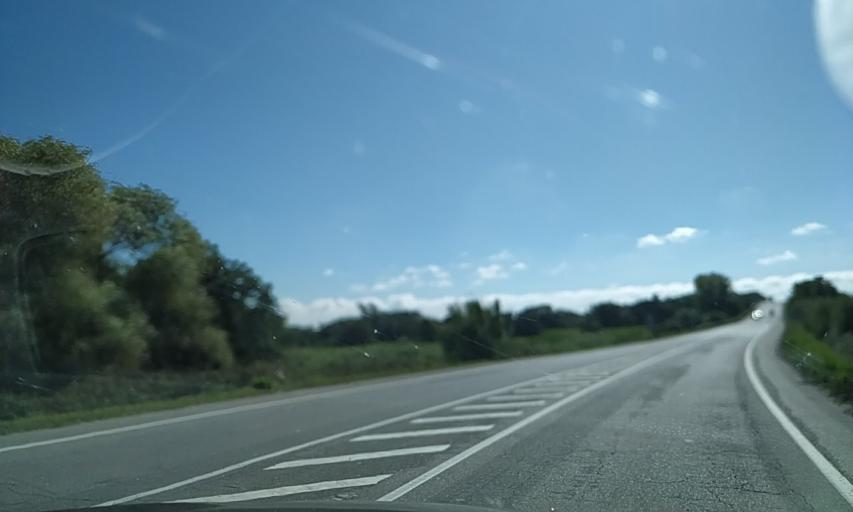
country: PT
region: Aveiro
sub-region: Estarreja
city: Salreu
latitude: 40.6853
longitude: -8.5599
